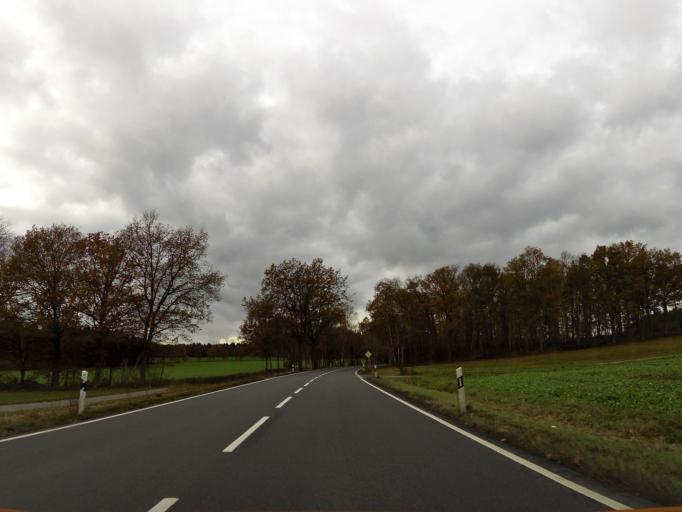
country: DE
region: Lower Saxony
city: Schnega
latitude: 52.9084
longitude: 10.9050
